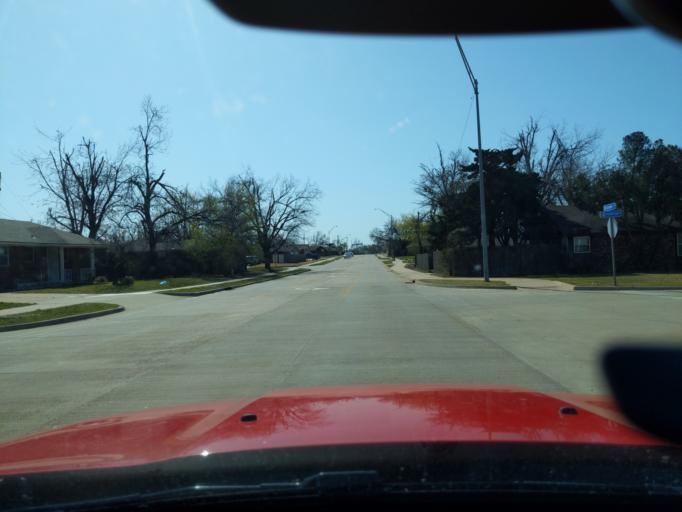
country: US
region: Oklahoma
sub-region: Cleveland County
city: Moore
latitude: 35.3461
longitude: -97.4888
